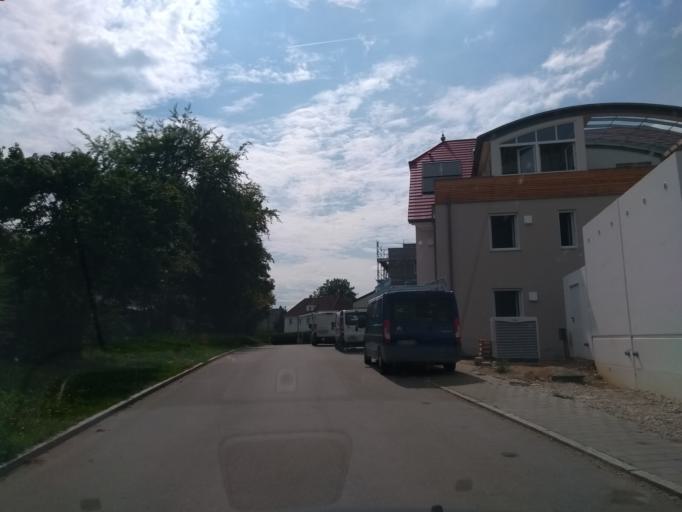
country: DE
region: Bavaria
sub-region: Upper Bavaria
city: Markt Indersdorf
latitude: 48.3666
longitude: 11.3778
